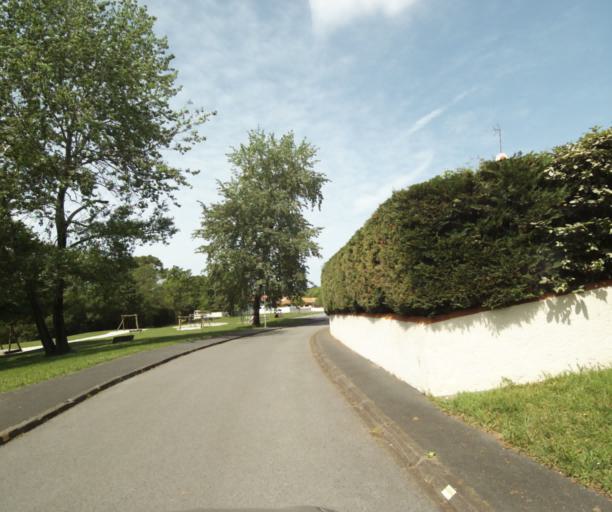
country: FR
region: Aquitaine
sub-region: Departement des Pyrenees-Atlantiques
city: Mouguerre
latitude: 43.4613
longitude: -1.4356
